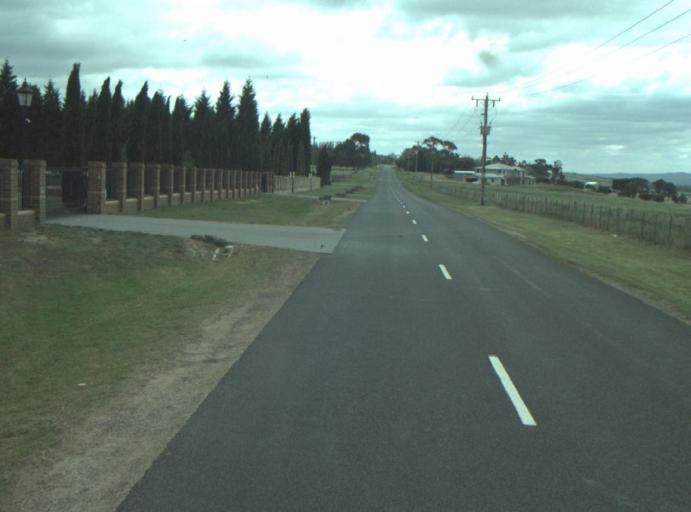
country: AU
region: Victoria
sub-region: Greater Geelong
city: Bell Post Hill
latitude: -38.0790
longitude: 144.3271
